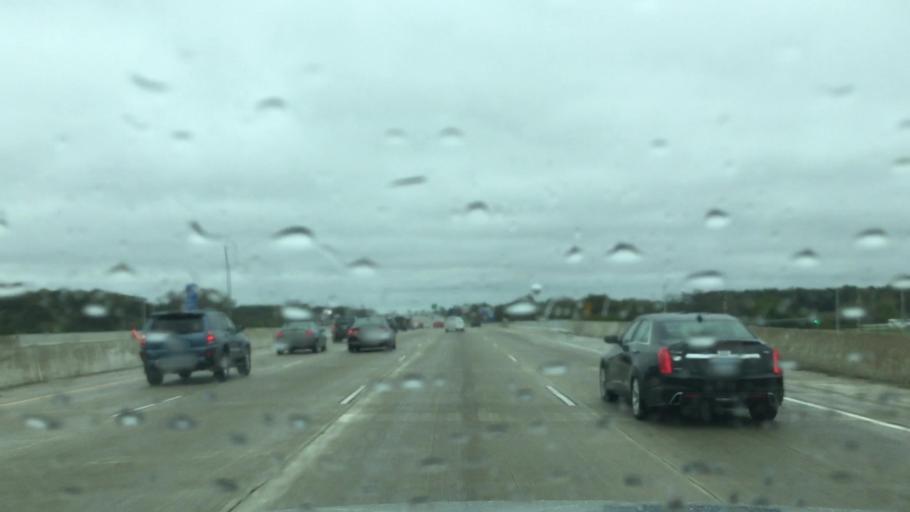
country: US
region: Wisconsin
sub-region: Kenosha County
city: Pleasant Prairie
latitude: 42.5907
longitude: -87.9530
